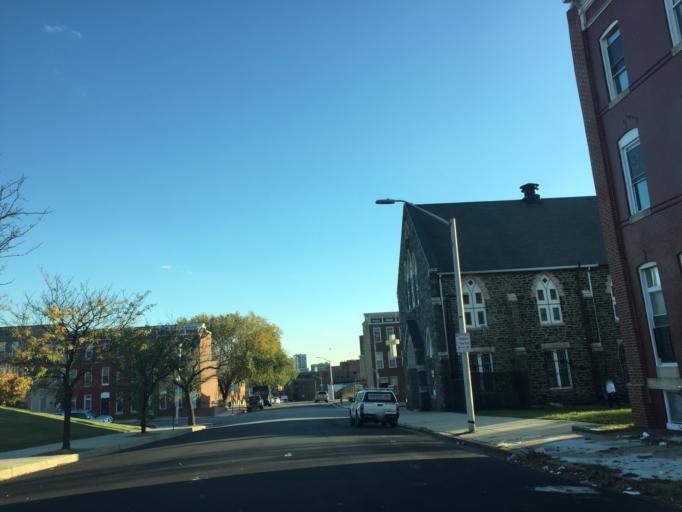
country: US
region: Maryland
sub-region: City of Baltimore
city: Baltimore
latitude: 39.3033
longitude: -76.6065
